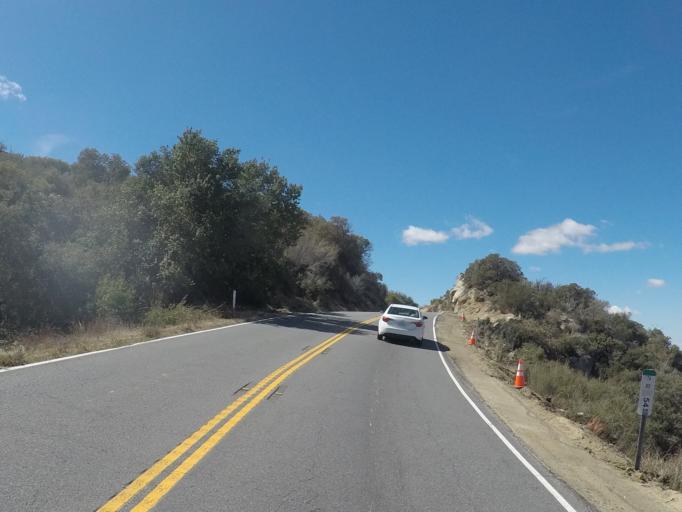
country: US
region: California
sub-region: Riverside County
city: Idyllwild-Pine Cove
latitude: 33.7047
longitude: -116.7621
